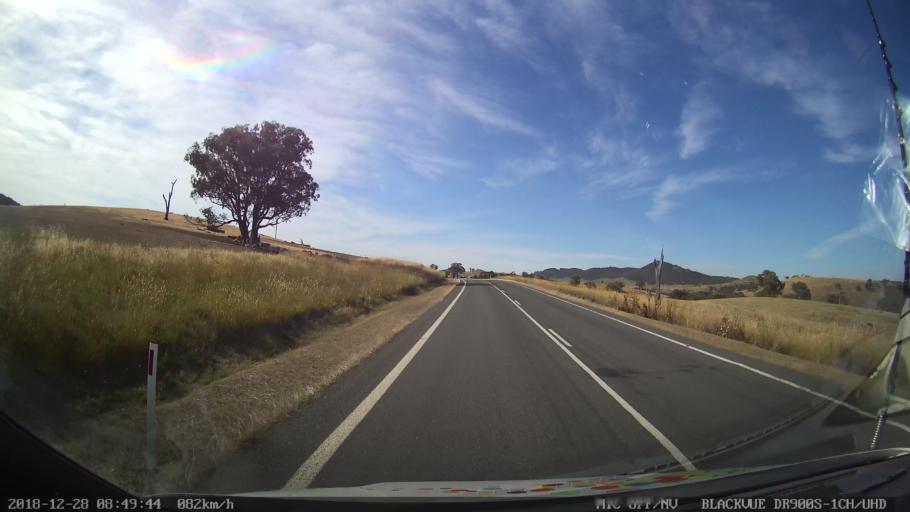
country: AU
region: New South Wales
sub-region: Upper Lachlan Shire
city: Crookwell
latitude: -34.0490
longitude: 149.3378
